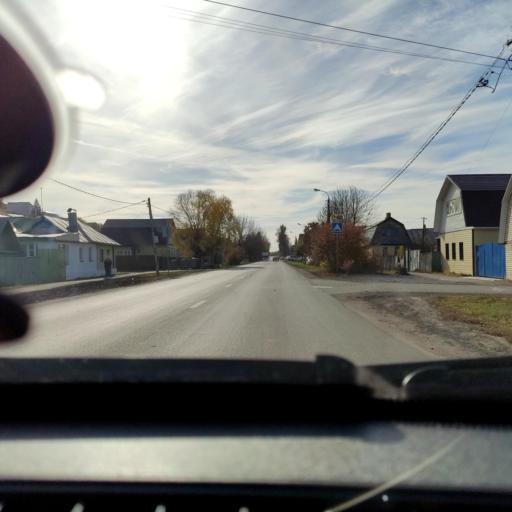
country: RU
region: Bashkortostan
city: Ufa
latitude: 54.7383
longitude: 55.9214
